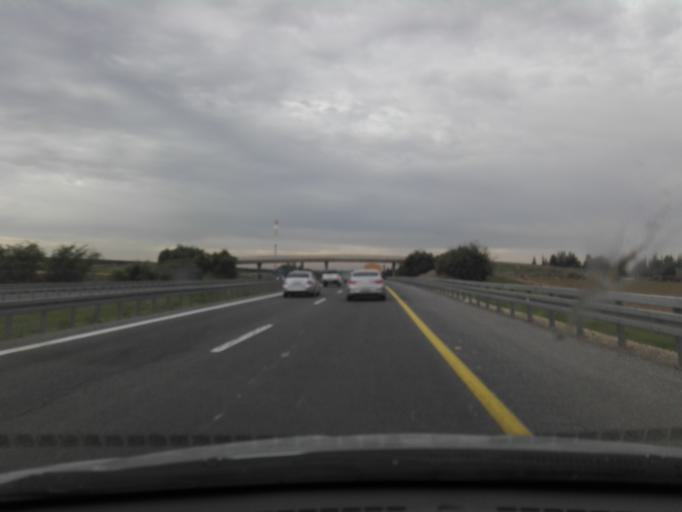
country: IL
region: Central District
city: Mazkeret Batya
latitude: 31.8686
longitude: 34.8741
